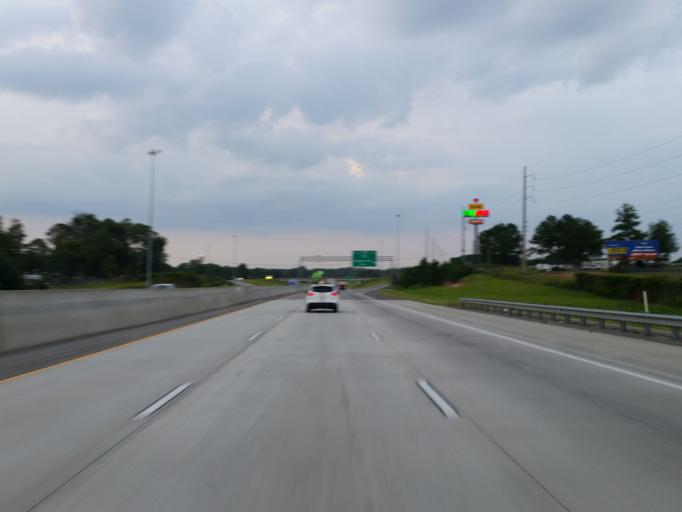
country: US
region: Georgia
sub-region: Tift County
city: Unionville
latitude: 31.4109
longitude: -83.5034
